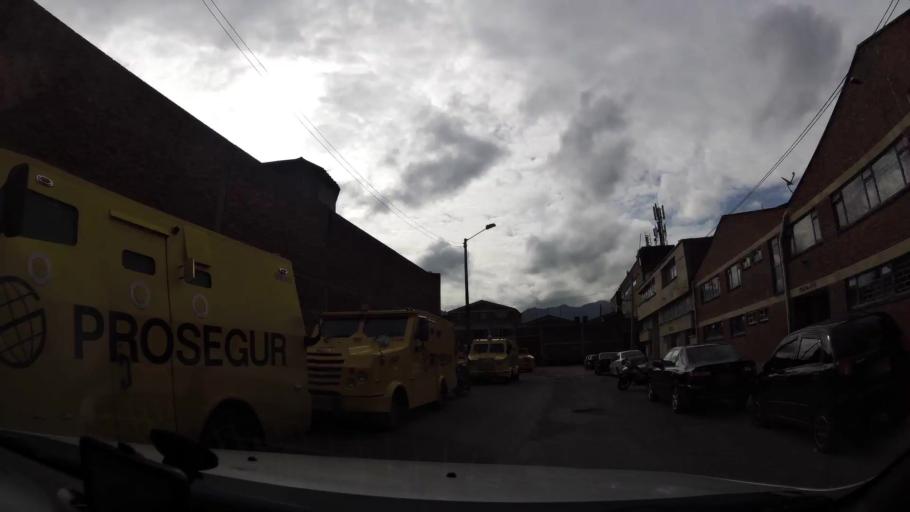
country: CO
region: Bogota D.C.
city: Bogota
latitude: 4.6253
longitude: -74.0966
